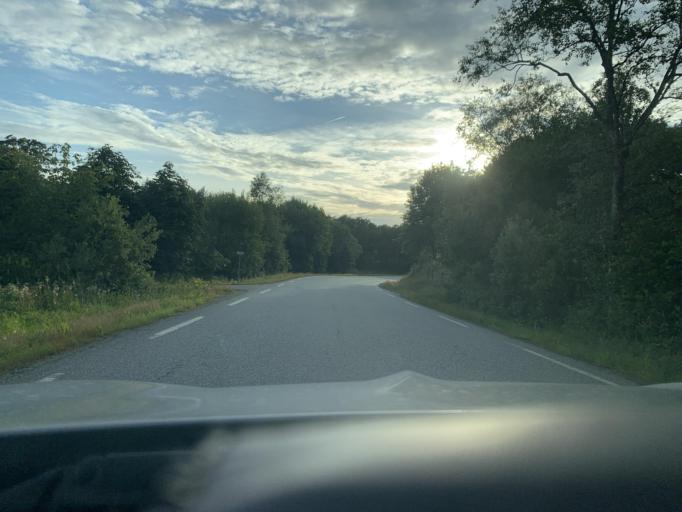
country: NO
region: Rogaland
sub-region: Ha
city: Naerbo
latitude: 58.6883
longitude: 5.7259
